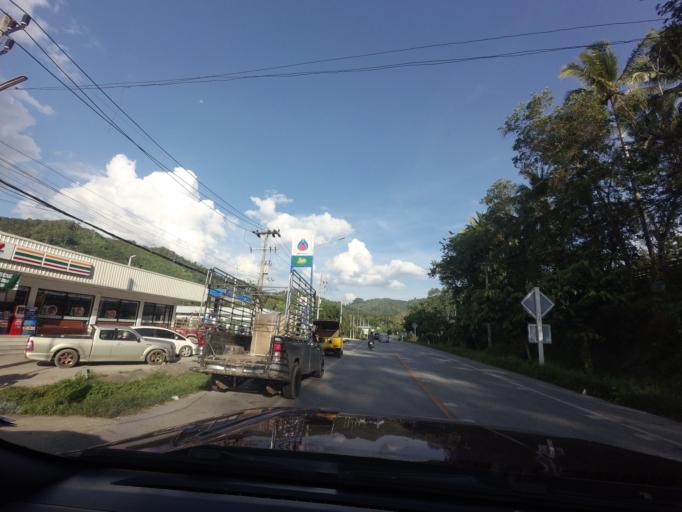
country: TH
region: Yala
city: Than To
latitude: 6.1605
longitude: 101.1880
